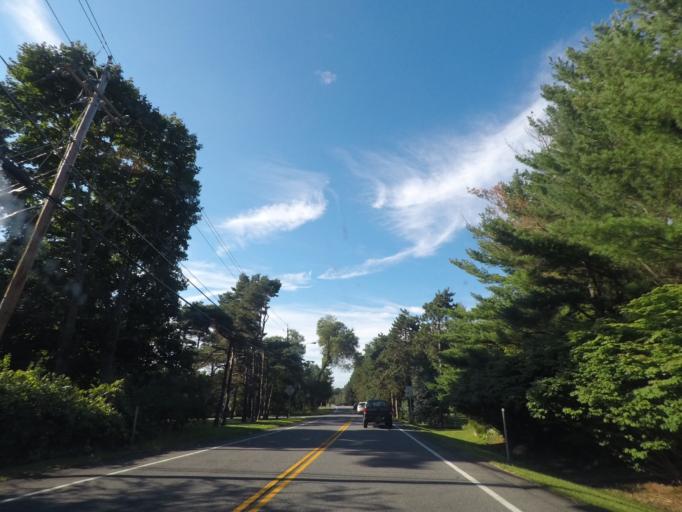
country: US
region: New York
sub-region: Albany County
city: West Albany
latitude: 42.7233
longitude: -73.7718
